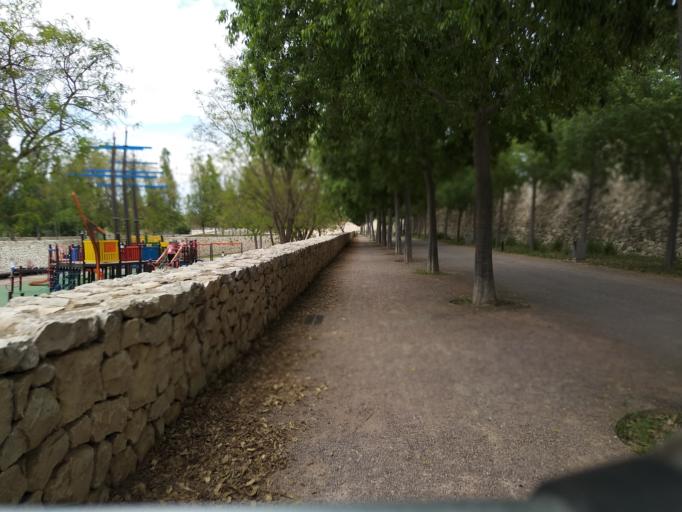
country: ES
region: Valencia
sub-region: Provincia de Valencia
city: Mislata
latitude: 39.4787
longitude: -0.4087
